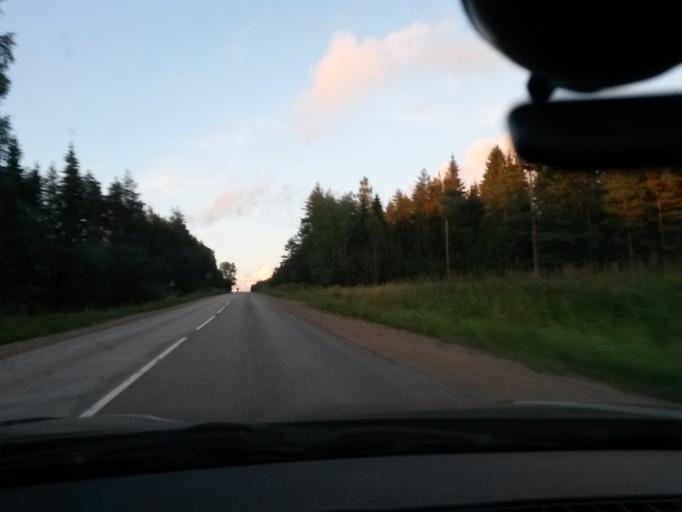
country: LV
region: Madonas Rajons
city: Madona
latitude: 56.8134
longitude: 26.1162
